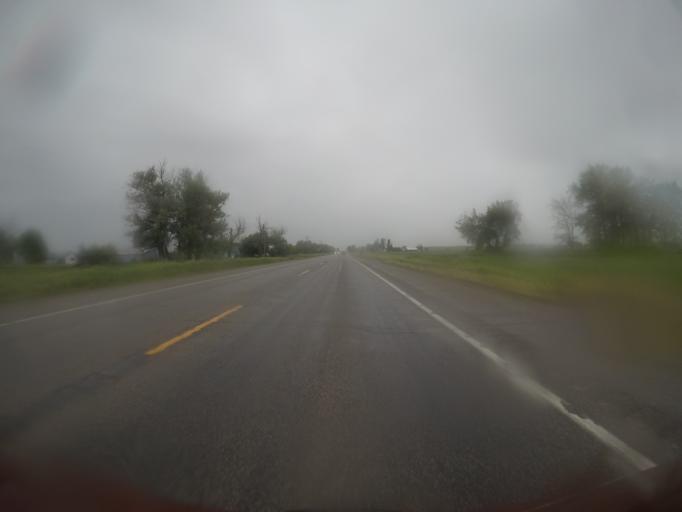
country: US
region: Montana
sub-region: Yellowstone County
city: Laurel
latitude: 45.5014
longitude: -108.8632
